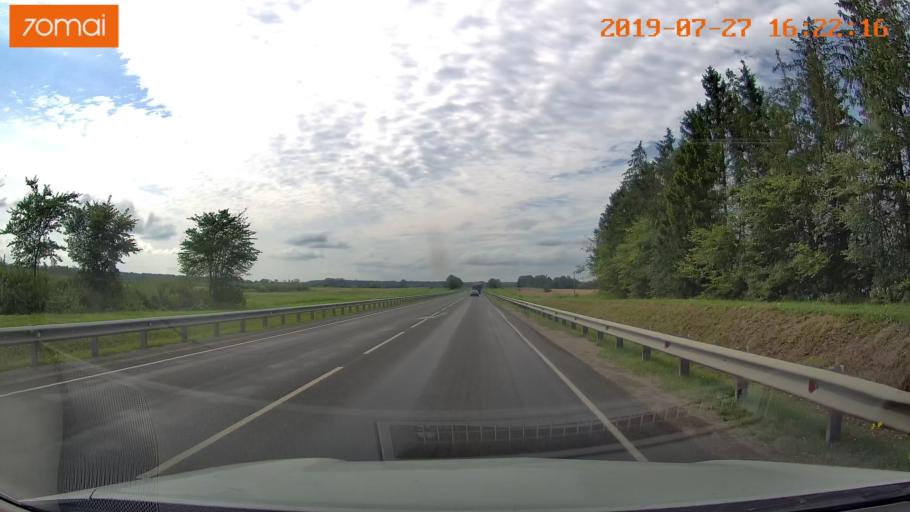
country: RU
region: Kaliningrad
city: Chernyakhovsk
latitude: 54.6270
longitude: 21.5000
